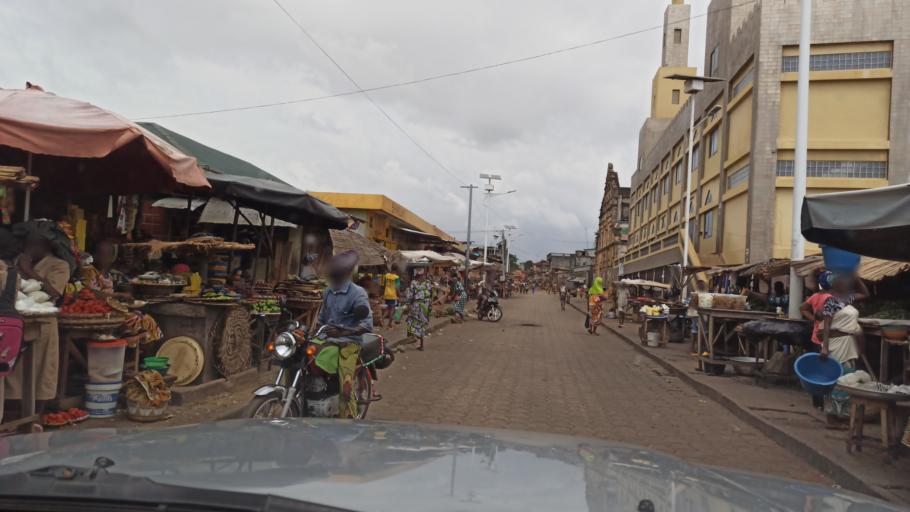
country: BJ
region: Queme
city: Porto-Novo
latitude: 6.4710
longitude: 2.6276
